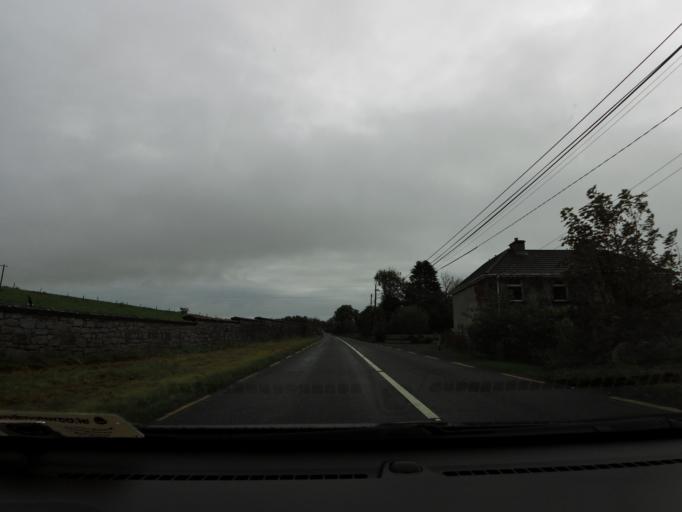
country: IE
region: Connaught
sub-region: County Galway
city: Tuam
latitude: 53.5695
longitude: -8.7881
